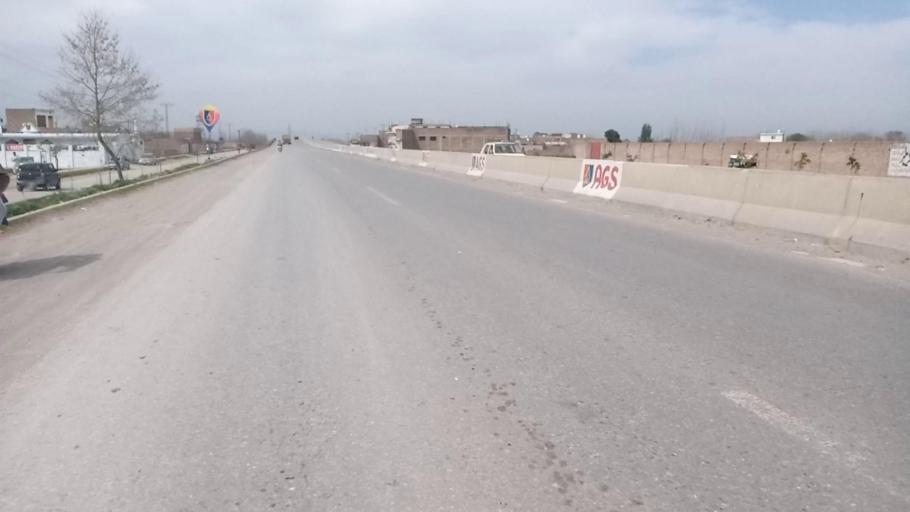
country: PK
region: Khyber Pakhtunkhwa
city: Peshawar
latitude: 34.0463
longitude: 71.6158
